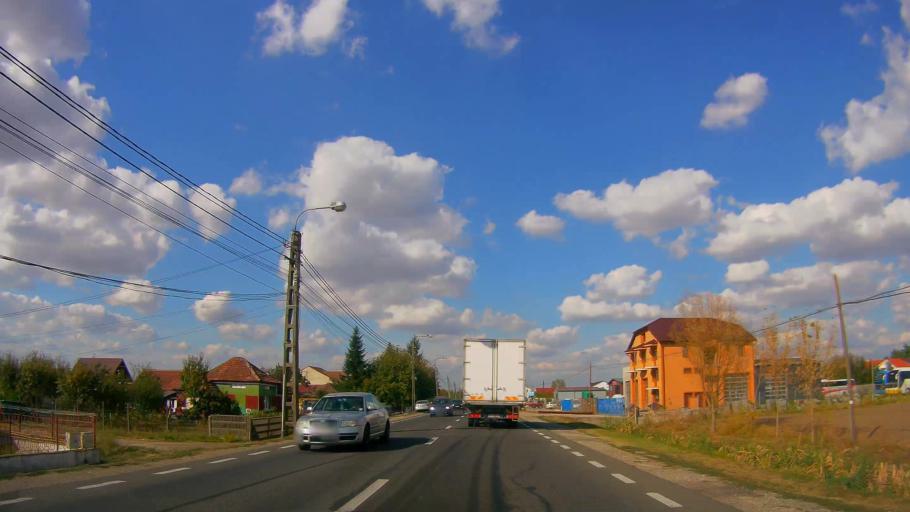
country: RO
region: Satu Mare
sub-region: Comuna Paulesti
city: Paulesti
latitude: 47.7518
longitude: 22.8831
